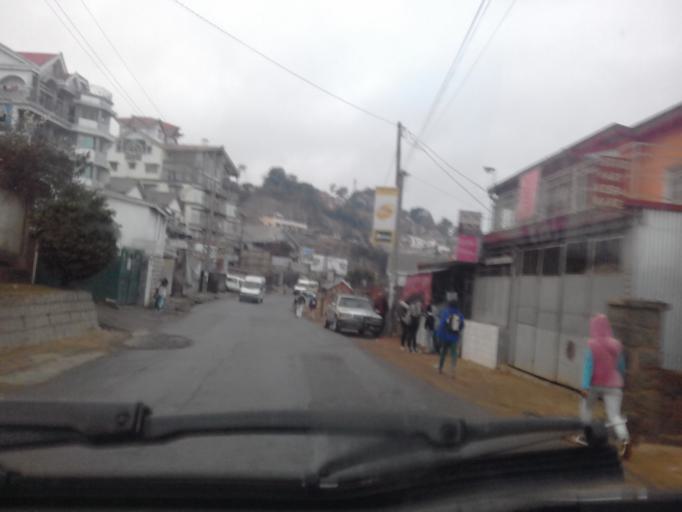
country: MG
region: Analamanga
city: Antananarivo
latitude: -18.8691
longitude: 47.5514
